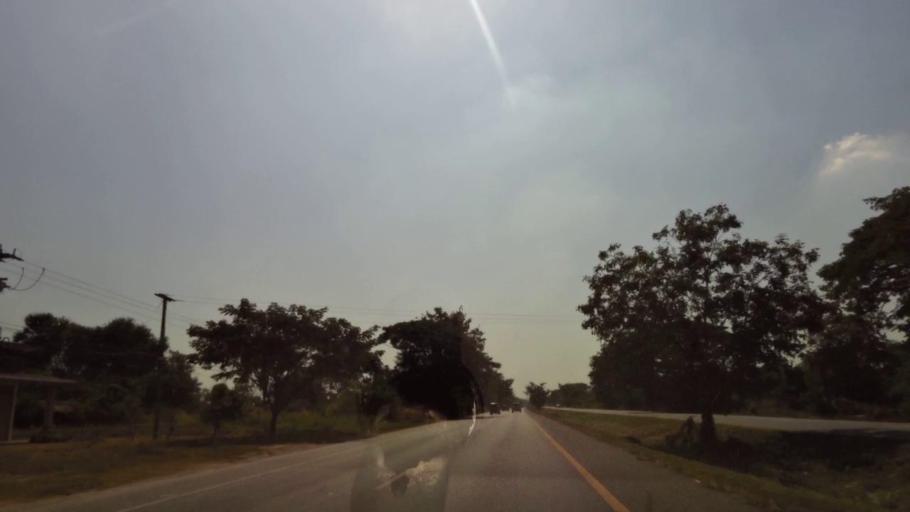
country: TH
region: Phichit
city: Wachira Barami
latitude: 16.3871
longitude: 100.1378
